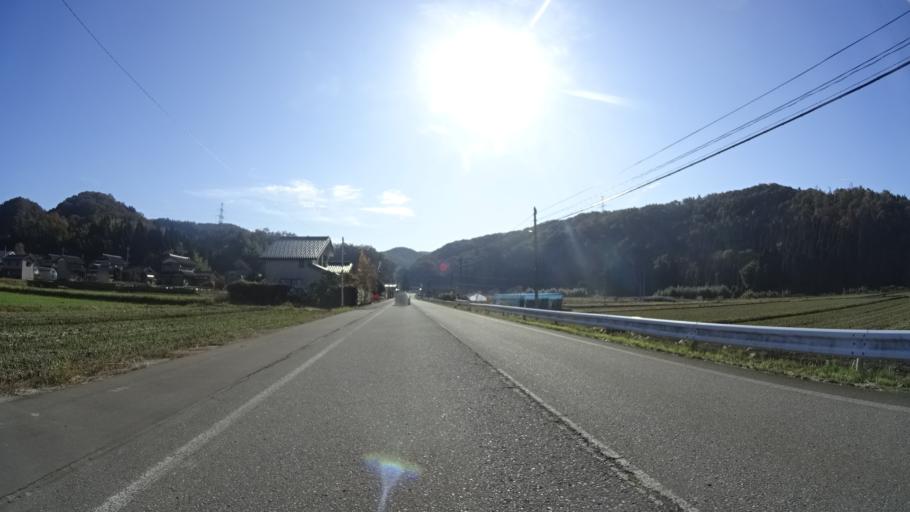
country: JP
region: Ishikawa
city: Komatsu
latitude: 36.3811
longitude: 136.5350
